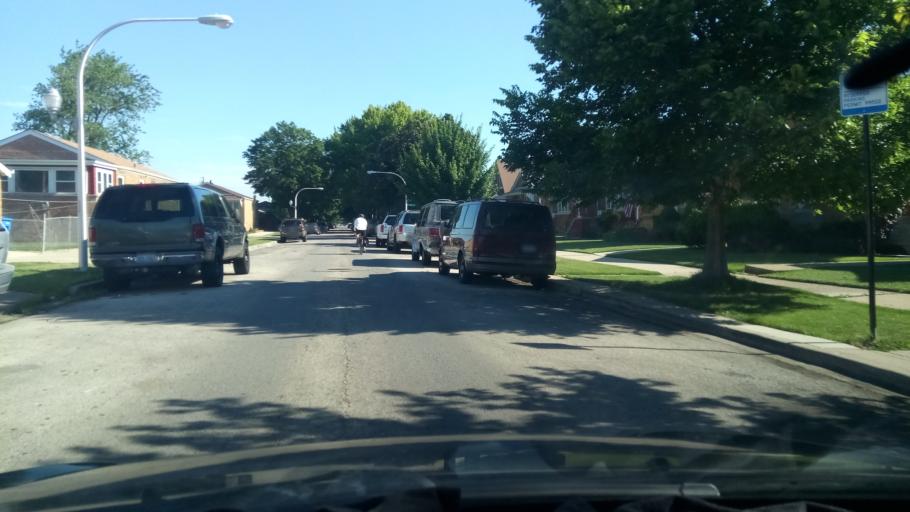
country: US
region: Illinois
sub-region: Cook County
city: Hometown
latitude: 41.7715
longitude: -87.7348
